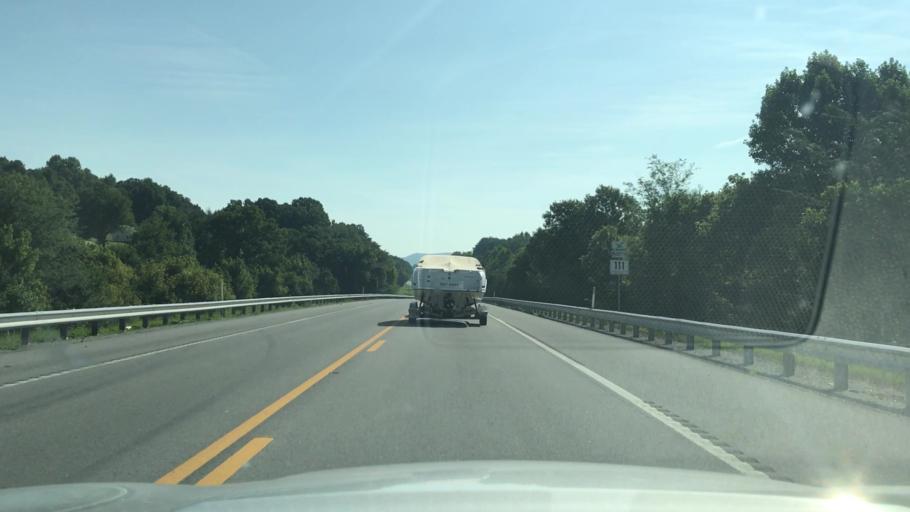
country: US
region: Tennessee
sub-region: Pickett County
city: Byrdstown
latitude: 36.6100
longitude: -85.1063
